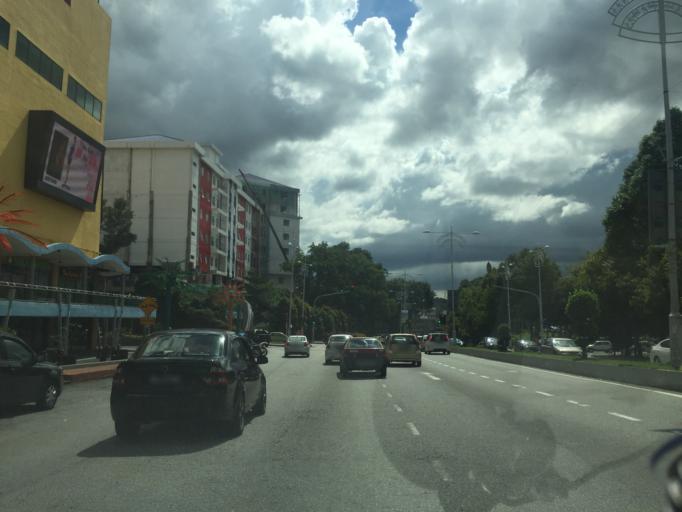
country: MY
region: Negeri Sembilan
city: Seremban
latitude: 2.7203
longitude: 101.9220
